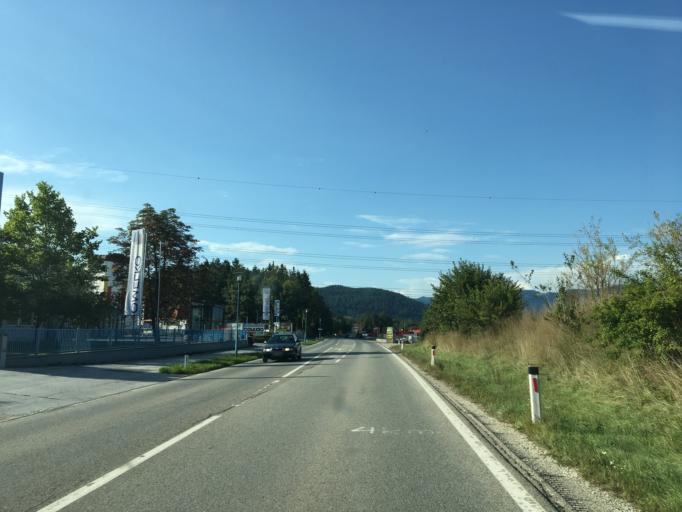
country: AT
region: Carinthia
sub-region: Politischer Bezirk Volkermarkt
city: Voelkermarkt
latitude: 46.6318
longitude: 14.6331
